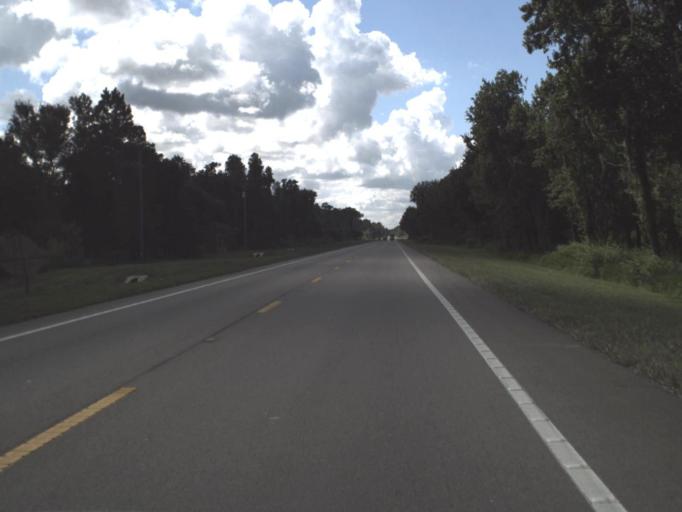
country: US
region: Florida
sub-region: Polk County
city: Kathleen
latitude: 28.2006
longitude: -82.0049
